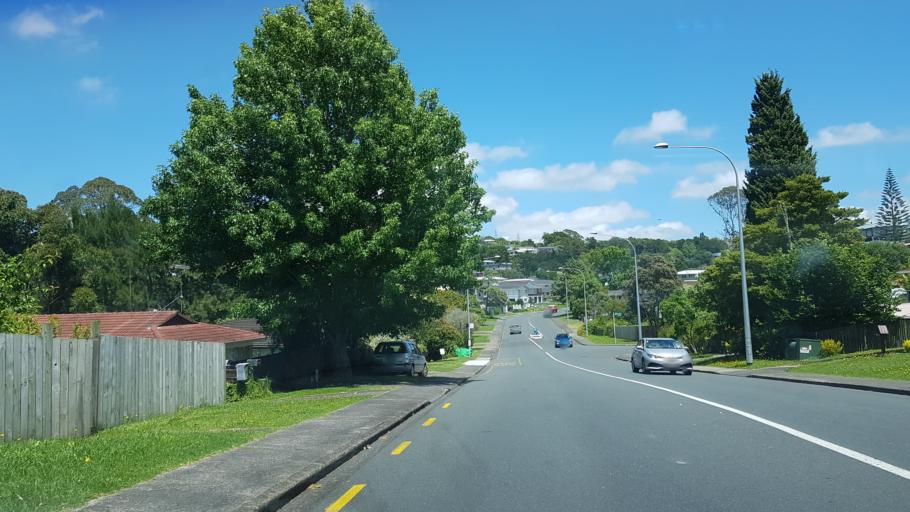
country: NZ
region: Auckland
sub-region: Auckland
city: North Shore
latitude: -36.7819
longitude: 174.7287
